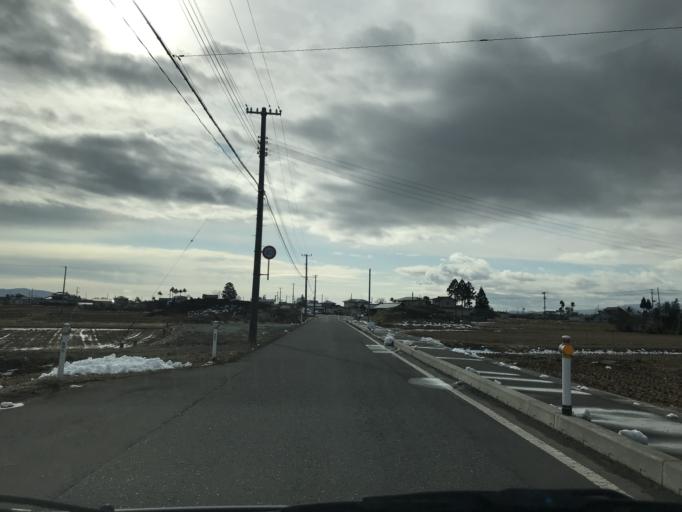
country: JP
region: Iwate
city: Mizusawa
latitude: 39.1739
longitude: 141.1307
